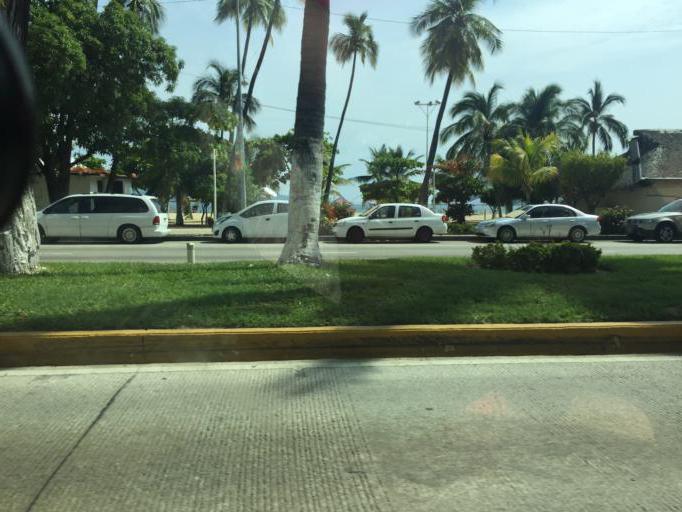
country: MX
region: Guerrero
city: Acapulco de Juarez
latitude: 16.8561
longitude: -99.8959
